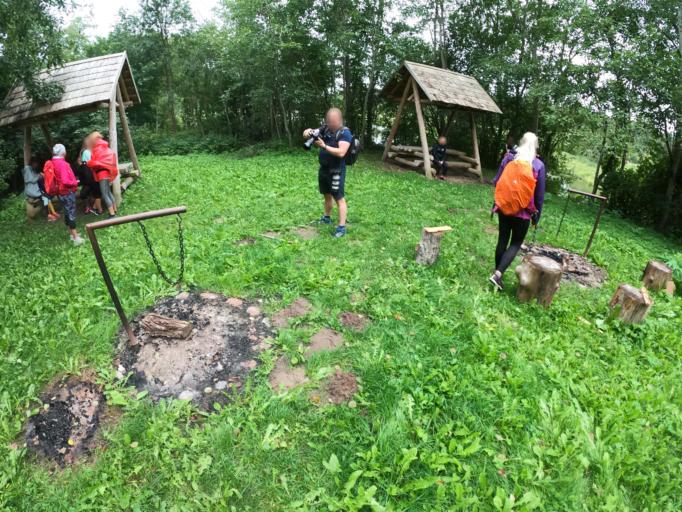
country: LV
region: Kuldigas Rajons
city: Kuldiga
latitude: 57.0095
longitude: 21.9794
